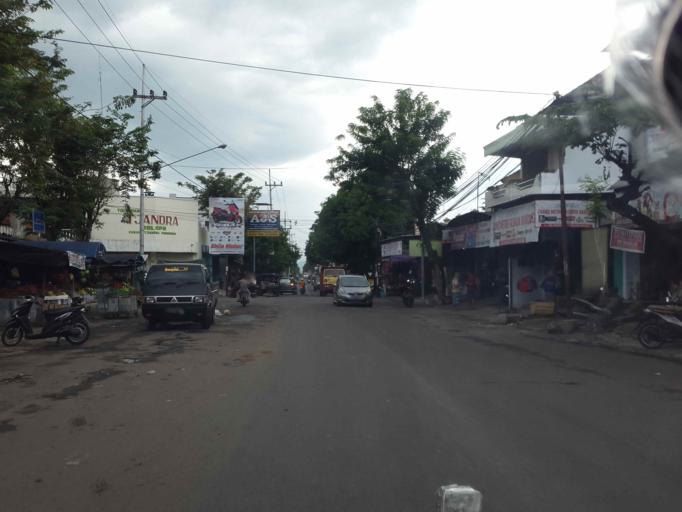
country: ID
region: East Java
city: Madiun
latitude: -7.7558
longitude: 111.5271
